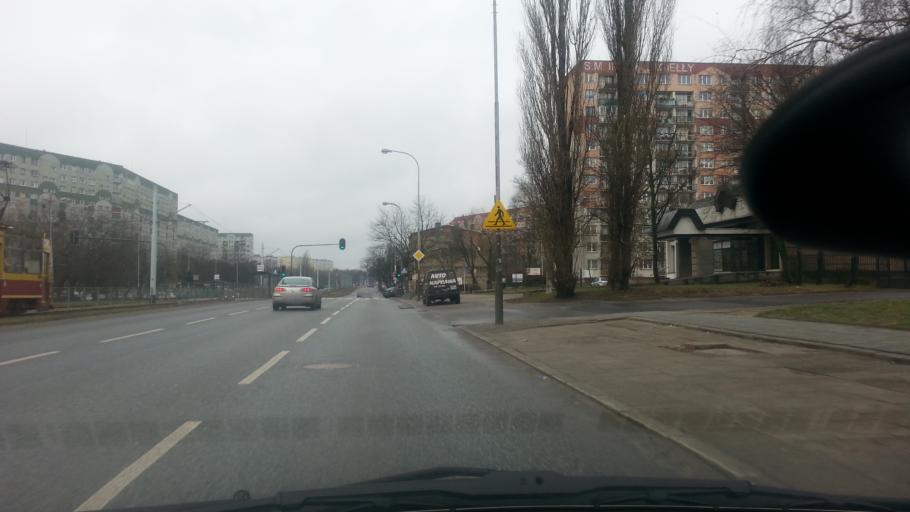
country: PL
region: Lodz Voivodeship
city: Lodz
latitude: 51.7925
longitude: 19.4482
